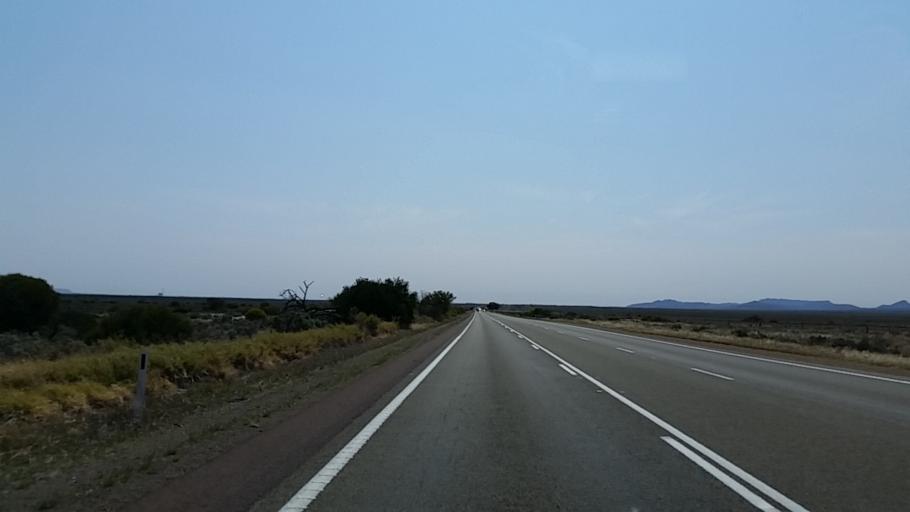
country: AU
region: South Australia
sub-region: Port Augusta
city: Port Augusta
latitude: -32.6802
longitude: 137.9373
